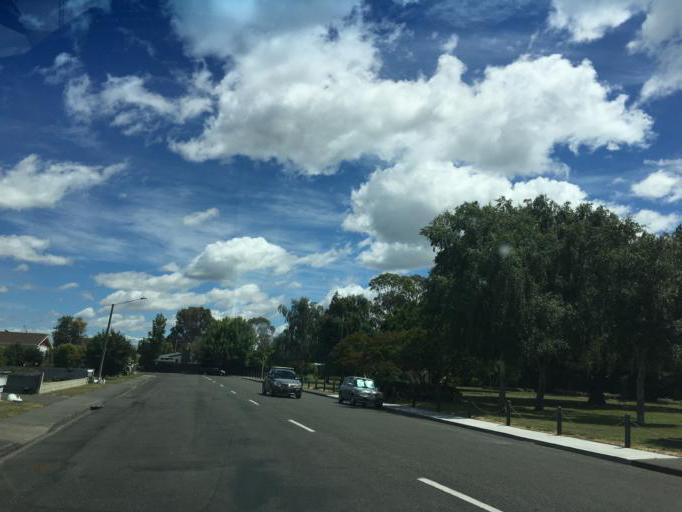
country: NZ
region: Hawke's Bay
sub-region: Hastings District
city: Hastings
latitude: -39.6472
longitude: 176.8605
